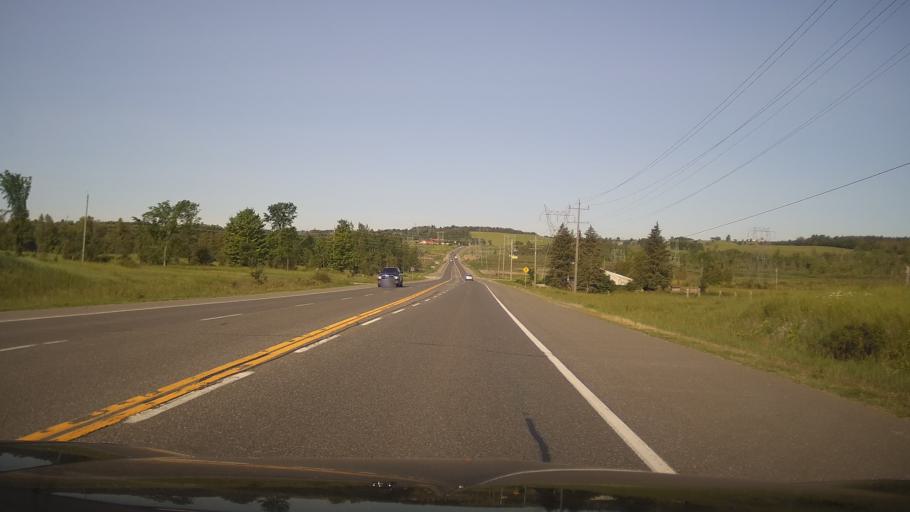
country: CA
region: Ontario
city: Peterborough
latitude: 44.3501
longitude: -78.0674
